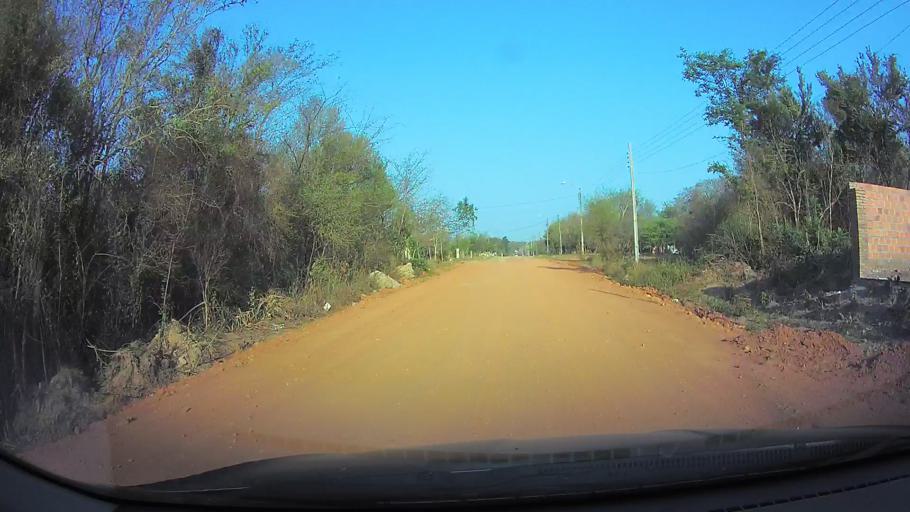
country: PY
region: Central
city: Limpio
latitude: -25.2174
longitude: -57.4940
